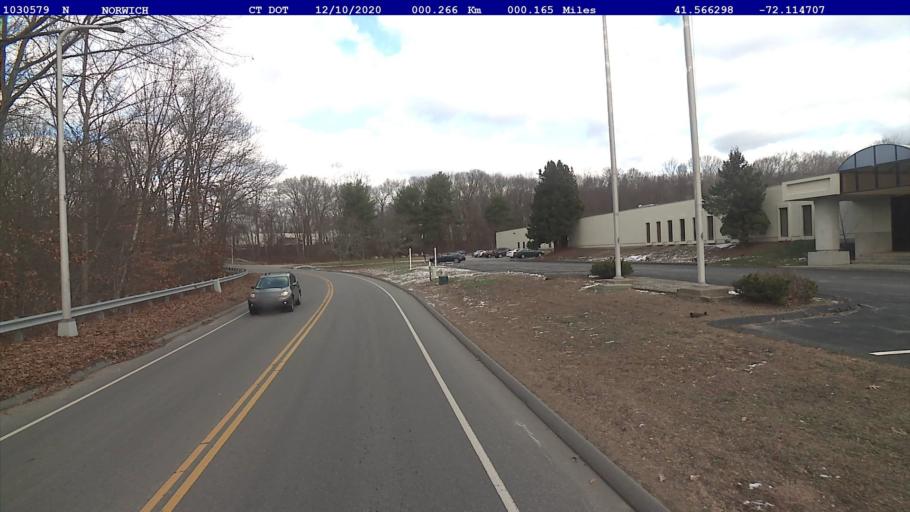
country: US
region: Connecticut
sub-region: New London County
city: Norwich
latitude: 41.5663
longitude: -72.1148
